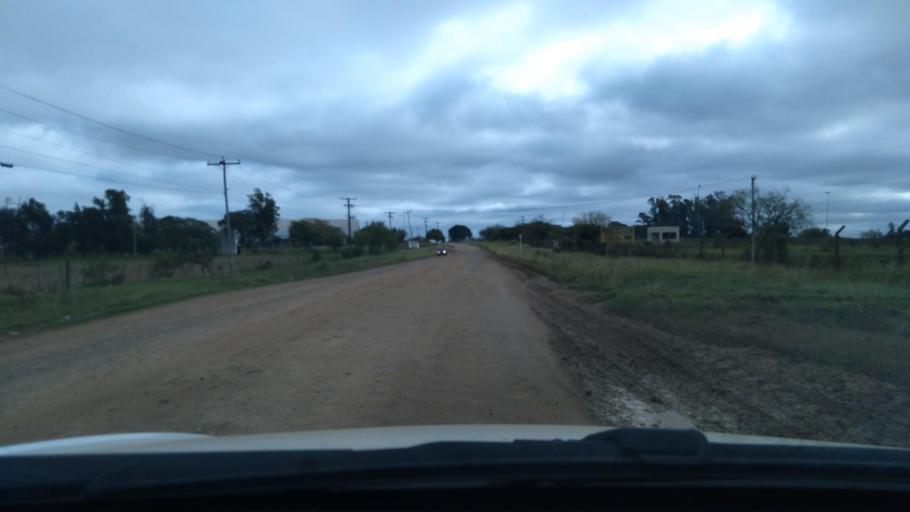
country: BR
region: Rio Grande do Sul
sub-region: Dom Pedrito
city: Dom Pedrito
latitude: -30.9838
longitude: -54.6400
